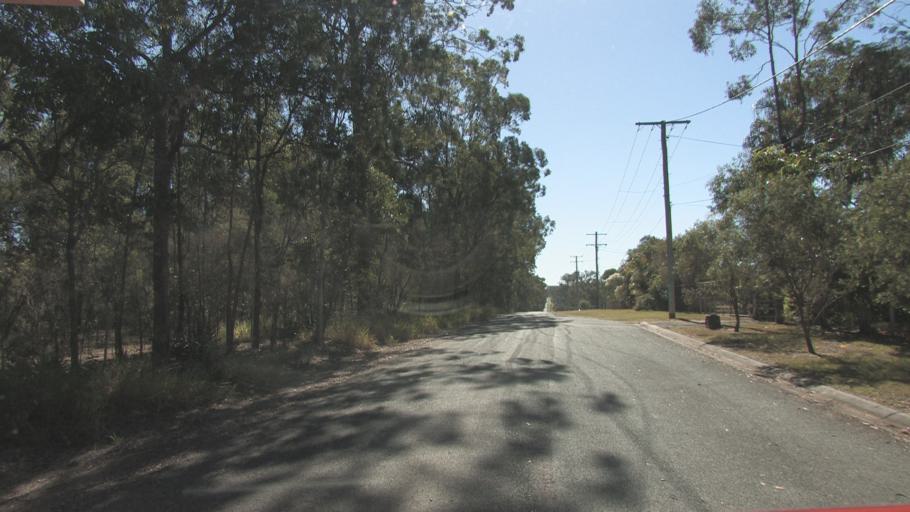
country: AU
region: Queensland
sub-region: Logan
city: Park Ridge South
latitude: -27.7019
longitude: 153.0034
